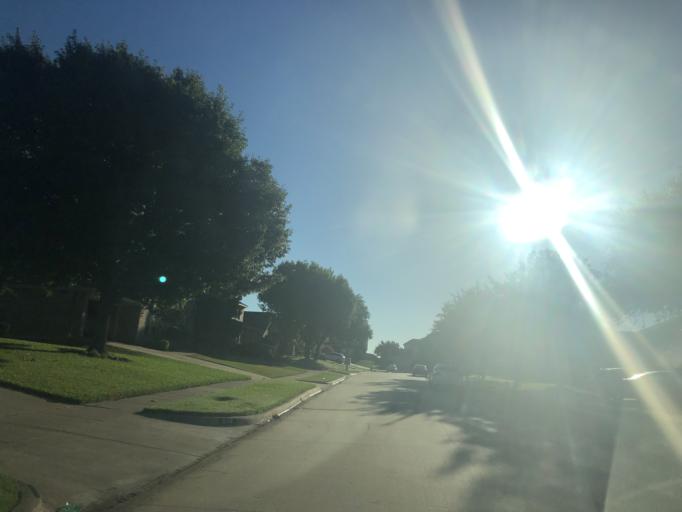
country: US
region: Texas
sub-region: Dallas County
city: Cedar Hill
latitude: 32.6593
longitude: -96.9986
